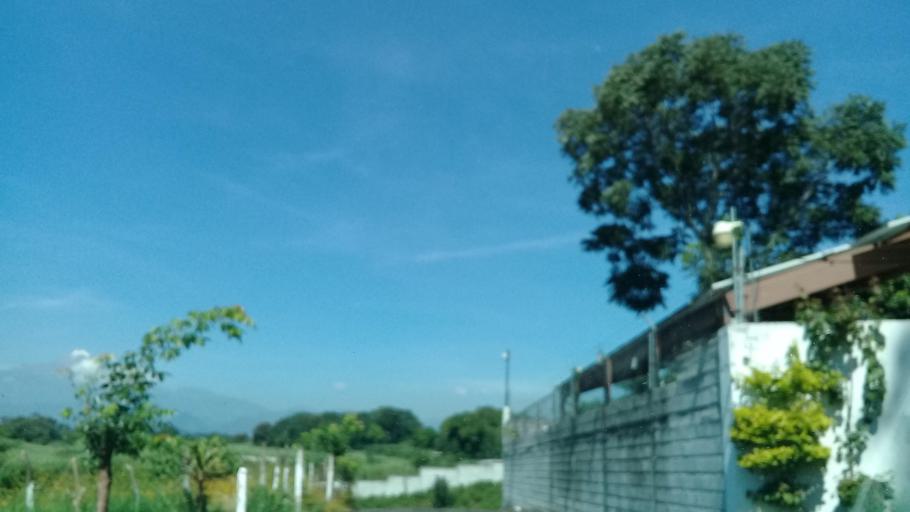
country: MX
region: Veracruz
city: Amatlan de los Reyes
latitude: 18.8548
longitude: -96.9228
